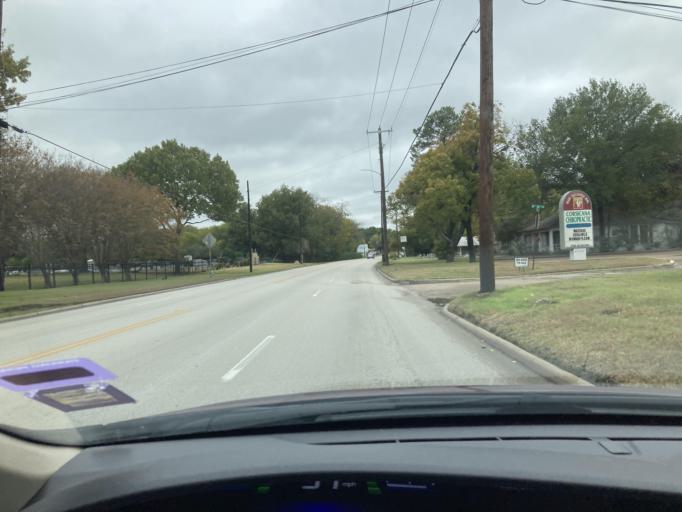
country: US
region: Texas
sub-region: Navarro County
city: Corsicana
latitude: 32.0857
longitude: -96.4896
